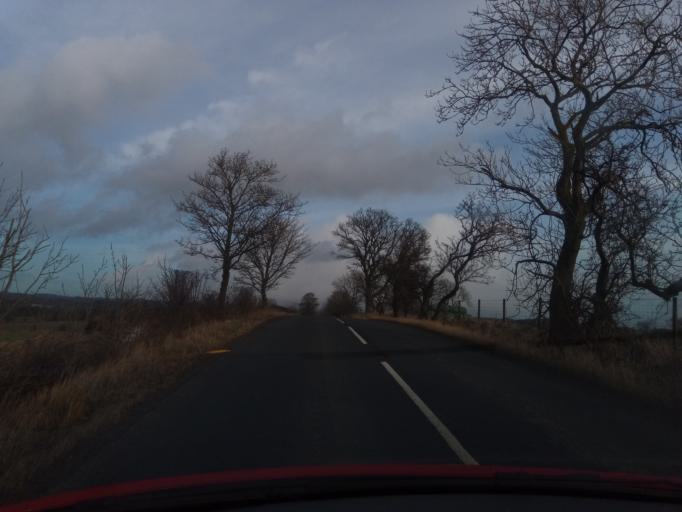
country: GB
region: England
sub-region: Northumberland
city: Rothley
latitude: 55.1295
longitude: -1.9829
